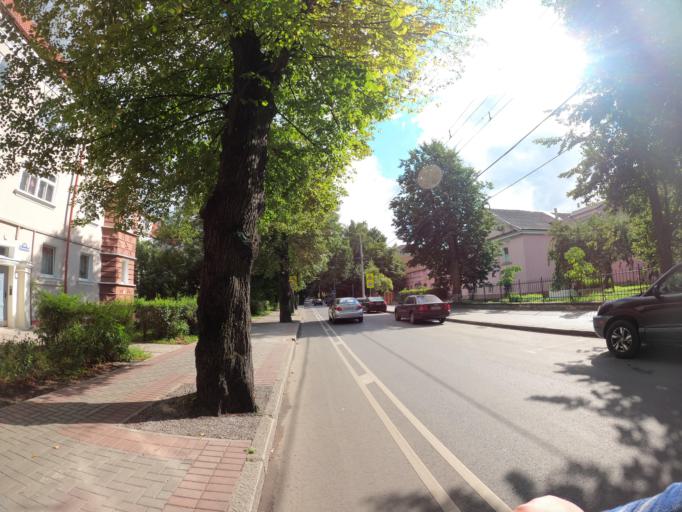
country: RU
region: Kaliningrad
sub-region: Gorod Kaliningrad
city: Kaliningrad
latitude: 54.7335
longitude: 20.4784
